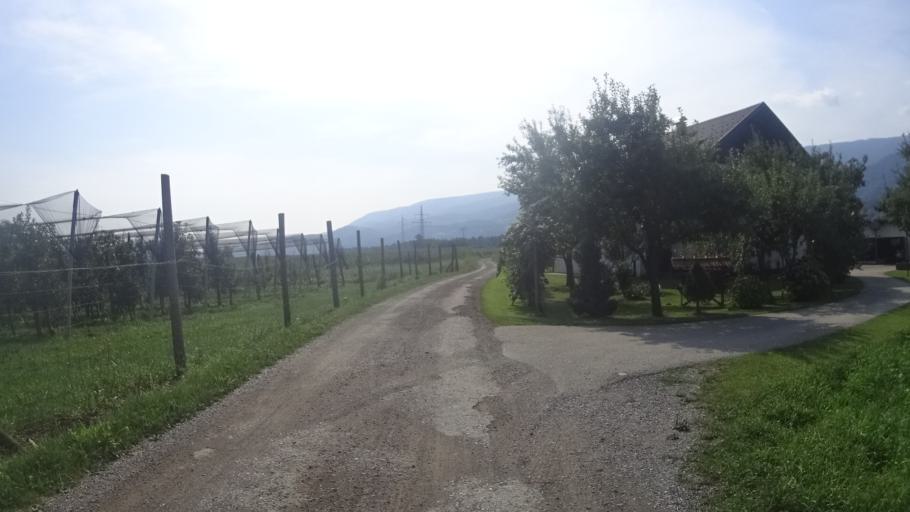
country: SI
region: Selnica ob Dravi
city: Selnica ob Dravi
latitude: 46.5464
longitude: 15.4720
